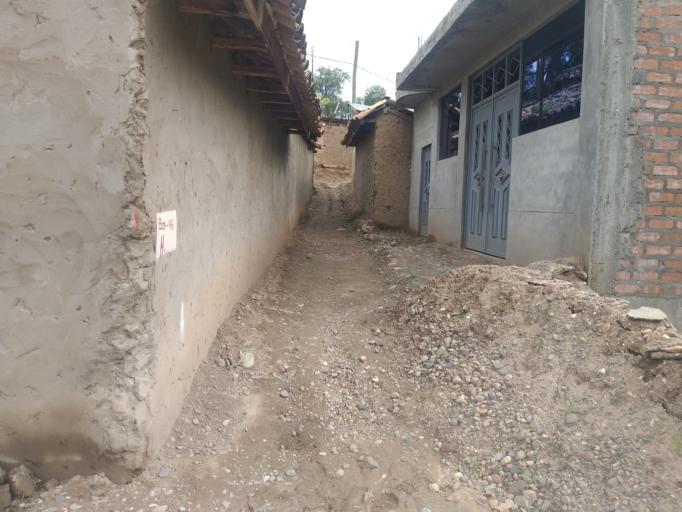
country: PE
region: Junin
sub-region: Provincia de Huancayo
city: Huayucachi
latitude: -12.1168
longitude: -75.2229
